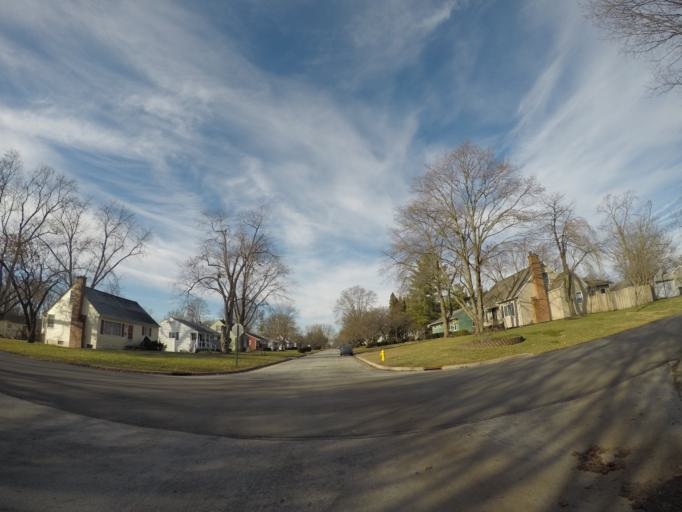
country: US
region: Ohio
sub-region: Franklin County
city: Upper Arlington
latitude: 40.0247
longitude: -83.0806
